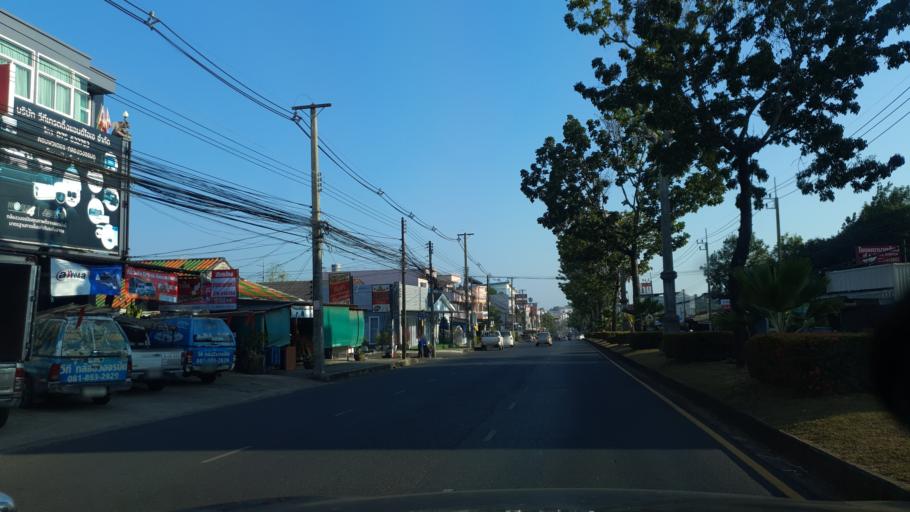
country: TH
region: Krabi
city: Krabi
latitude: 8.0753
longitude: 98.9100
